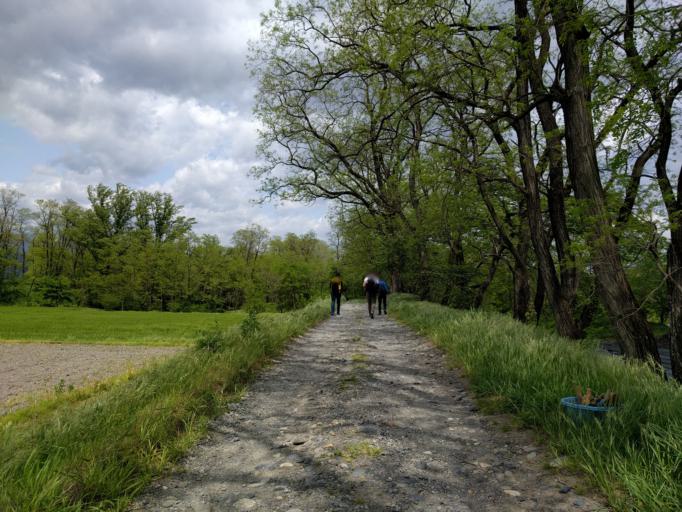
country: JP
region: Nagano
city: Hotaka
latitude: 36.3360
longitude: 137.9122
